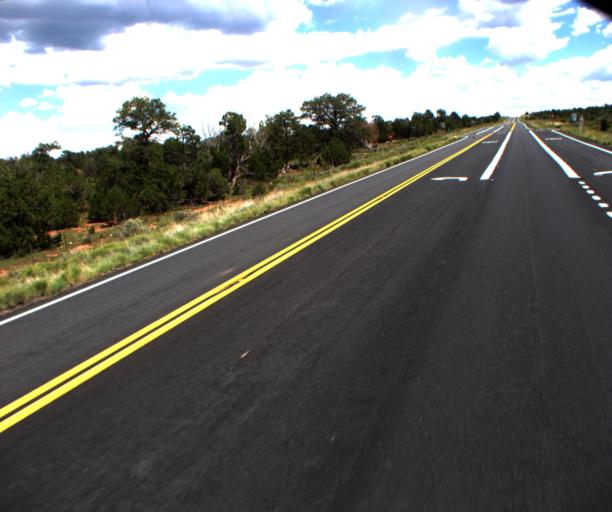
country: US
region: Arizona
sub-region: Coconino County
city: Parks
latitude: 35.6048
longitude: -112.0419
